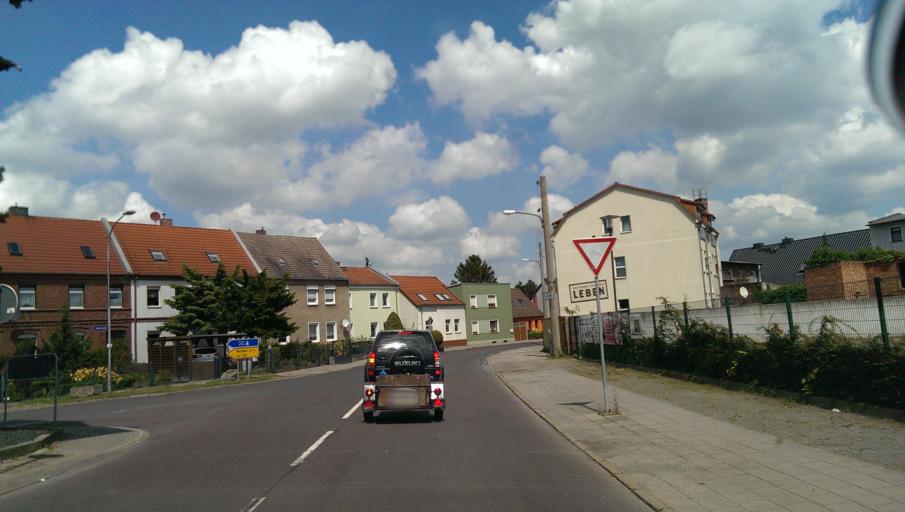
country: DE
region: Saxony-Anhalt
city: Schonebeck
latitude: 52.0011
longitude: 11.7140
